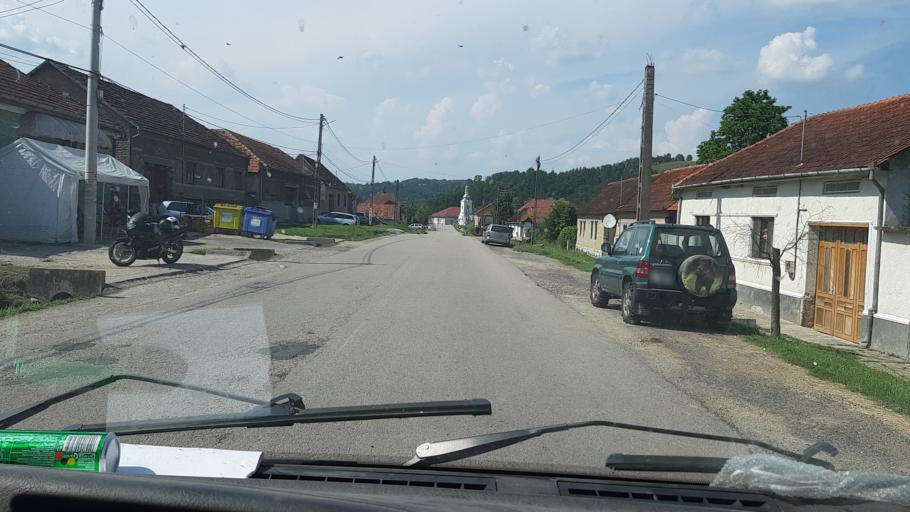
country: RO
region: Caras-Severin
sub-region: Comuna Ezeris
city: Ezeris
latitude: 45.4096
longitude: 21.8860
